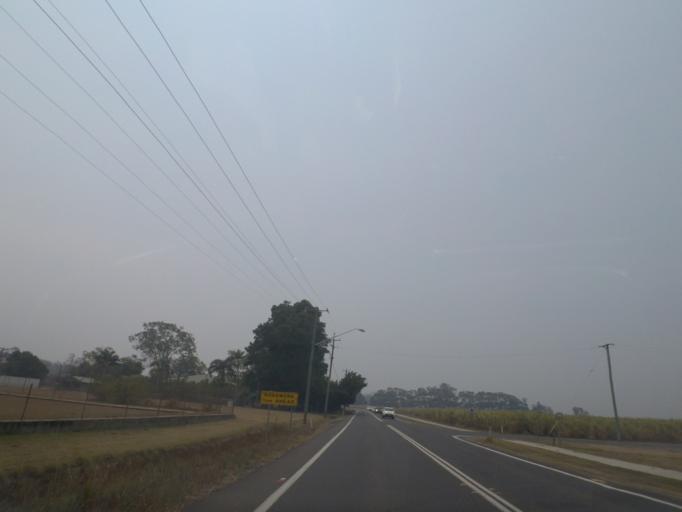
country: AU
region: New South Wales
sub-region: Richmond Valley
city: Evans Head
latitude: -29.0088
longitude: 153.4365
